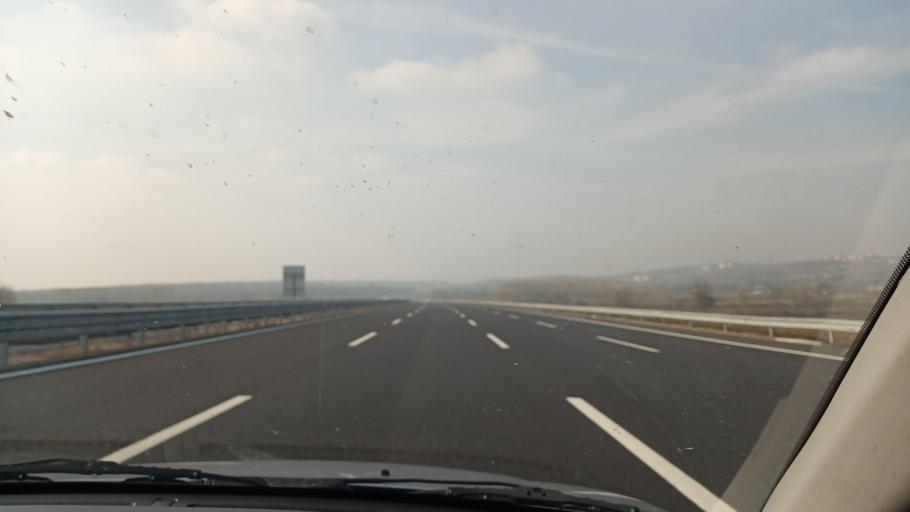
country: TR
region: Sakarya
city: Kazimpasa
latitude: 40.8441
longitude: 30.3245
